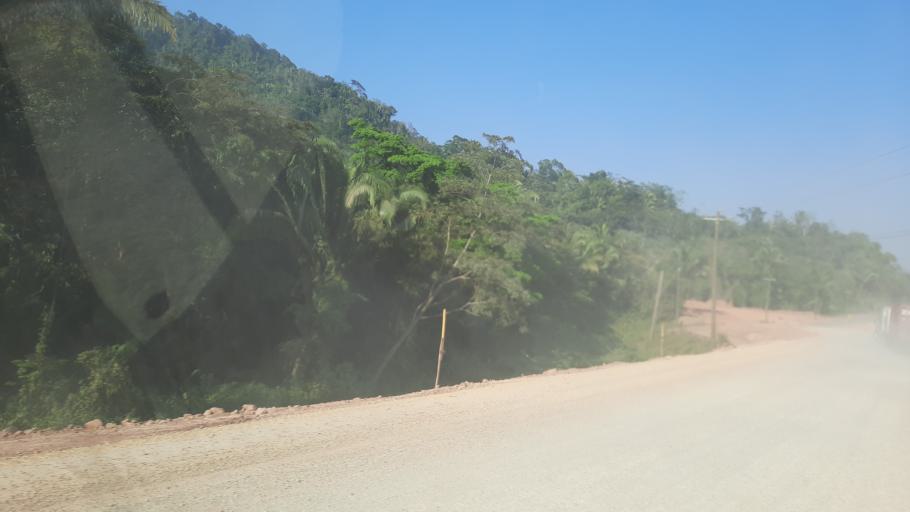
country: BZ
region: Cayo
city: Belmopan
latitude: 17.0560
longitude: -88.5842
